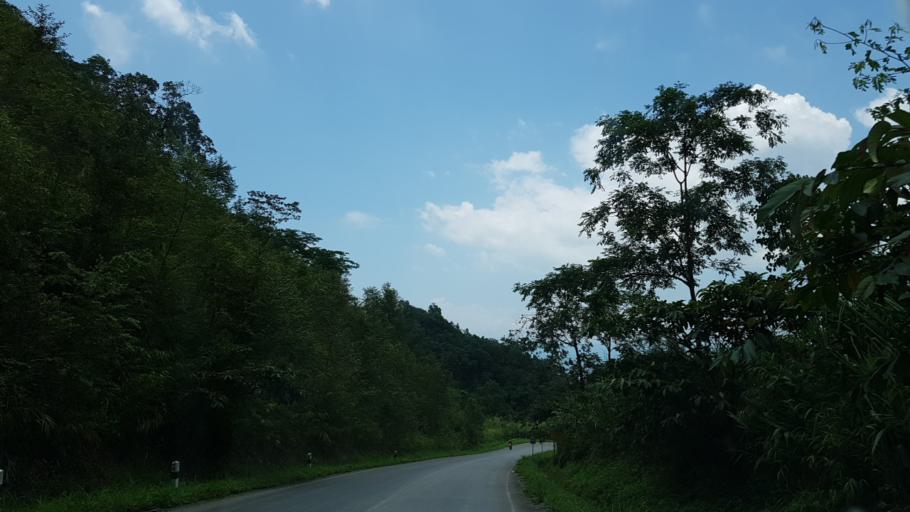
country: LA
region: Vientiane
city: Muang Kasi
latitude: 19.3776
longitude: 102.1581
